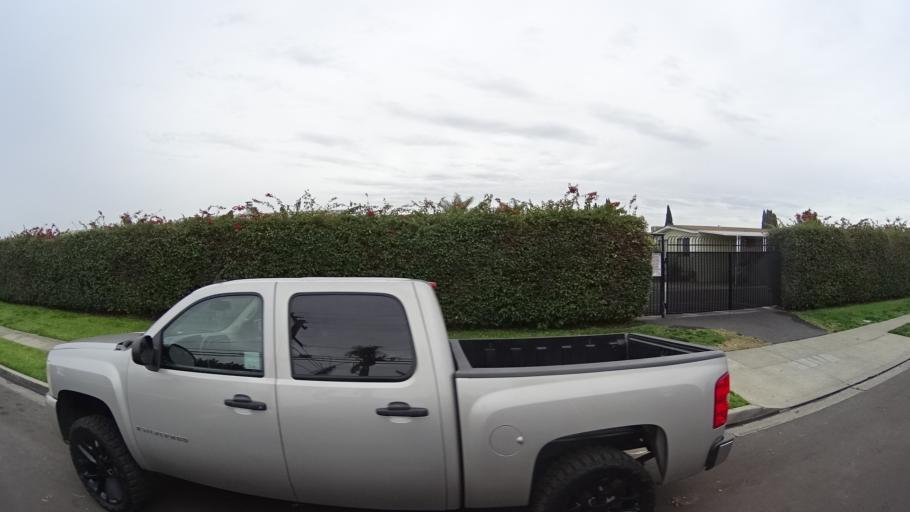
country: US
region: California
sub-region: Orange County
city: Midway City
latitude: 33.7420
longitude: -117.9863
